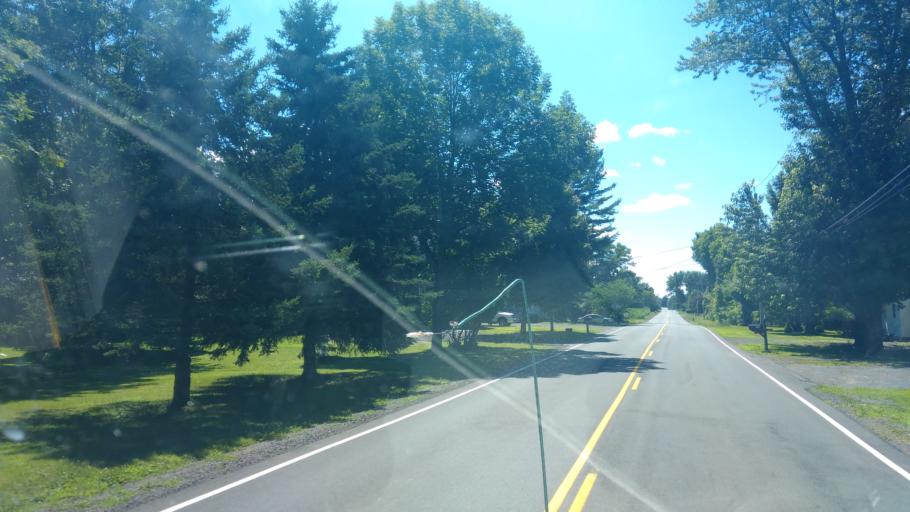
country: US
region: New York
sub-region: Wayne County
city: Sodus
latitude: 43.2045
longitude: -77.0259
